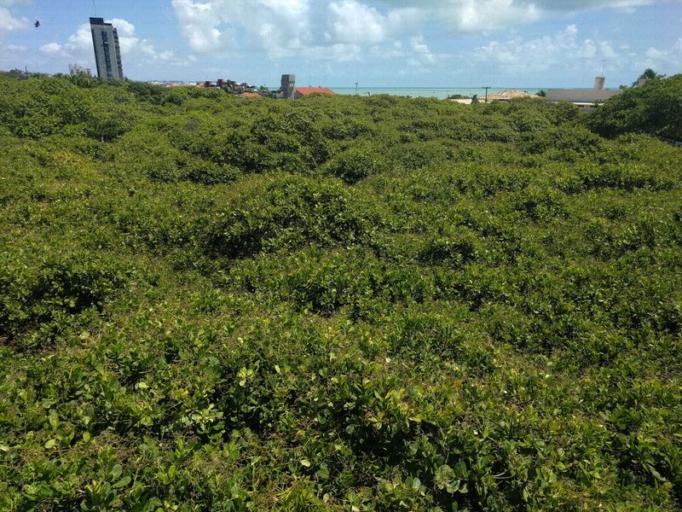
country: BR
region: Rio Grande do Norte
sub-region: Nisia Floresta
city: Nisia Floresta
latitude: -5.9792
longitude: -35.1232
